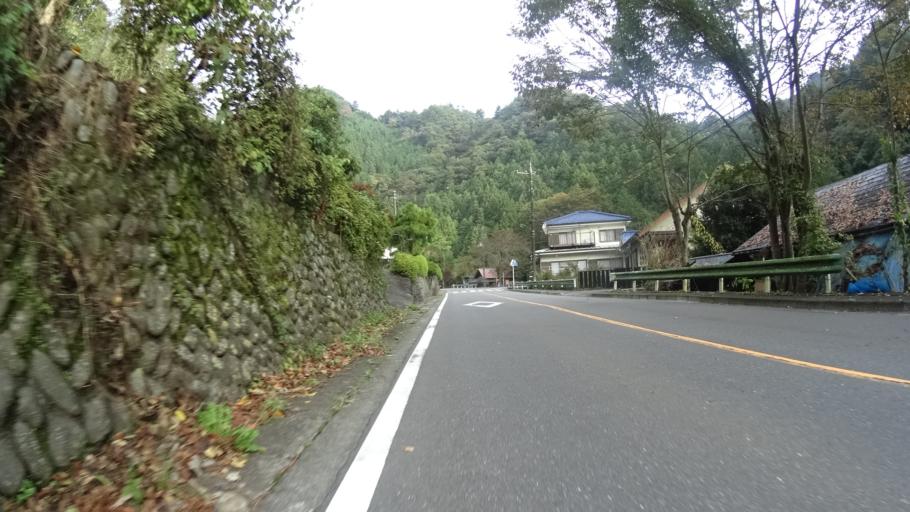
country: JP
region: Yamanashi
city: Uenohara
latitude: 35.7040
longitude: 139.1250
